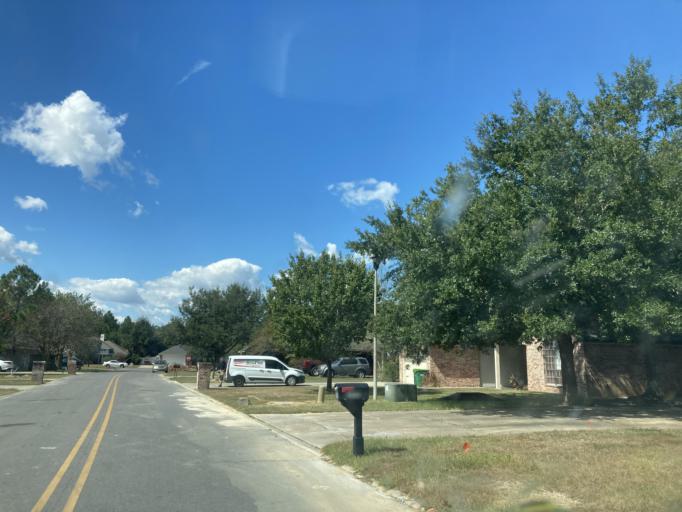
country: US
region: Mississippi
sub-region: Jackson County
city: Saint Martin
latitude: 30.4402
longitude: -88.8644
